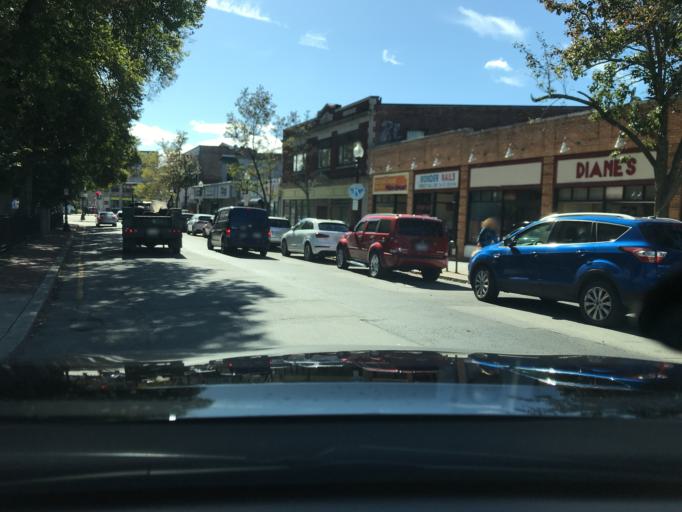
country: US
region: Massachusetts
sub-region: Suffolk County
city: Jamaica Plain
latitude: 42.2868
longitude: -71.1287
